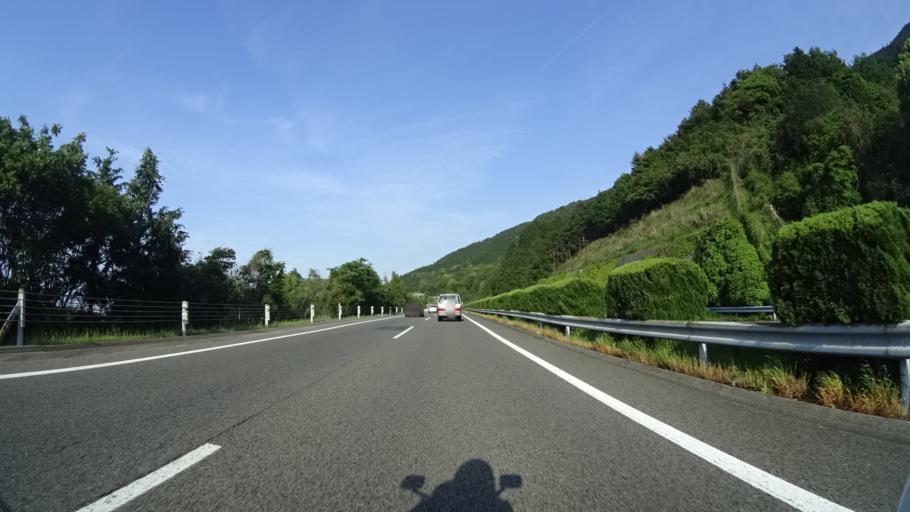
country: JP
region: Ehime
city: Niihama
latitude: 33.9505
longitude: 133.4310
